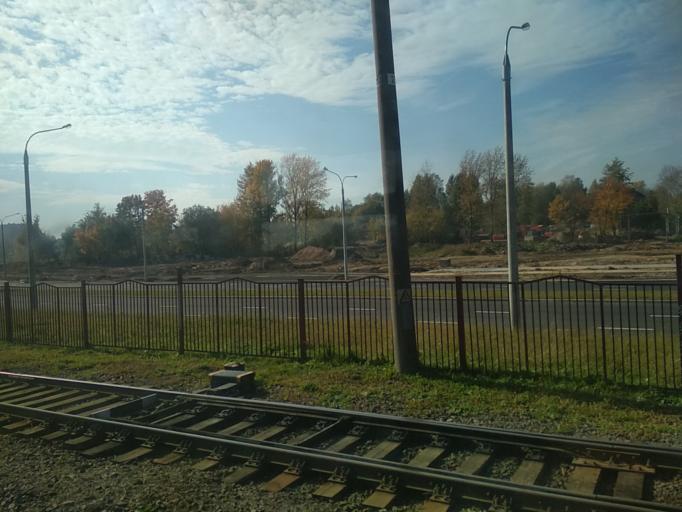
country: BY
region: Minsk
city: Syenitsa
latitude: 53.8603
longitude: 27.5590
